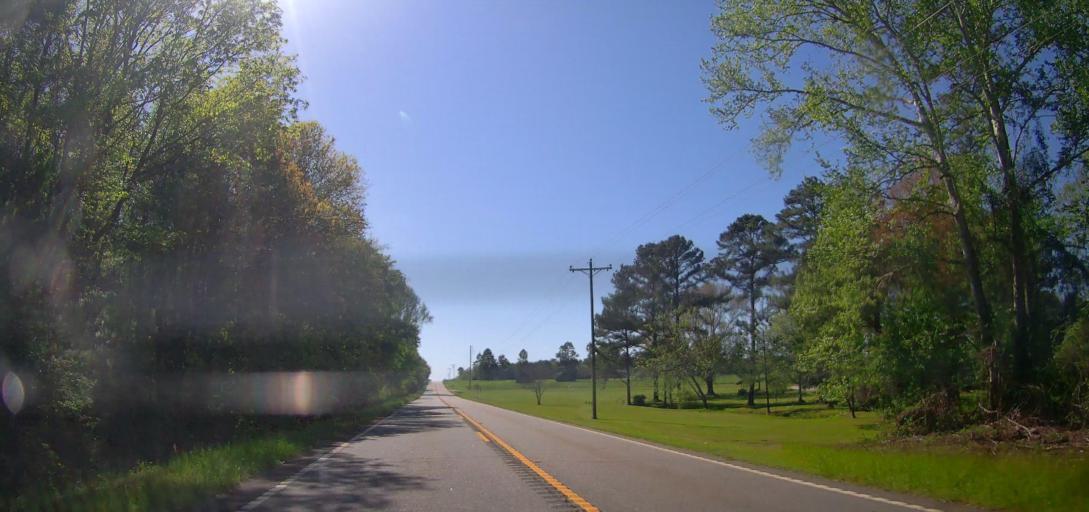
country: US
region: Georgia
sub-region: Dooly County
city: Unadilla
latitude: 32.2600
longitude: -83.6858
